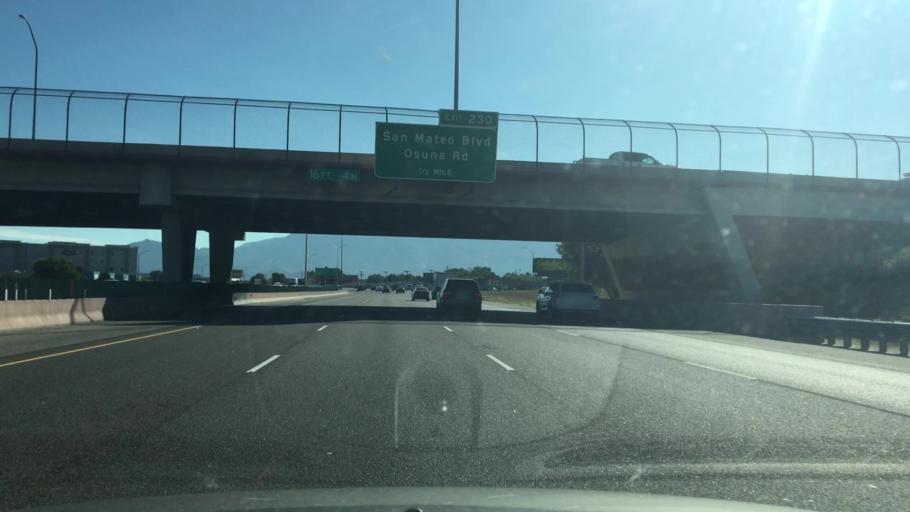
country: US
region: New Mexico
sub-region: Bernalillo County
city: North Valley
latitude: 35.1414
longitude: -106.5953
